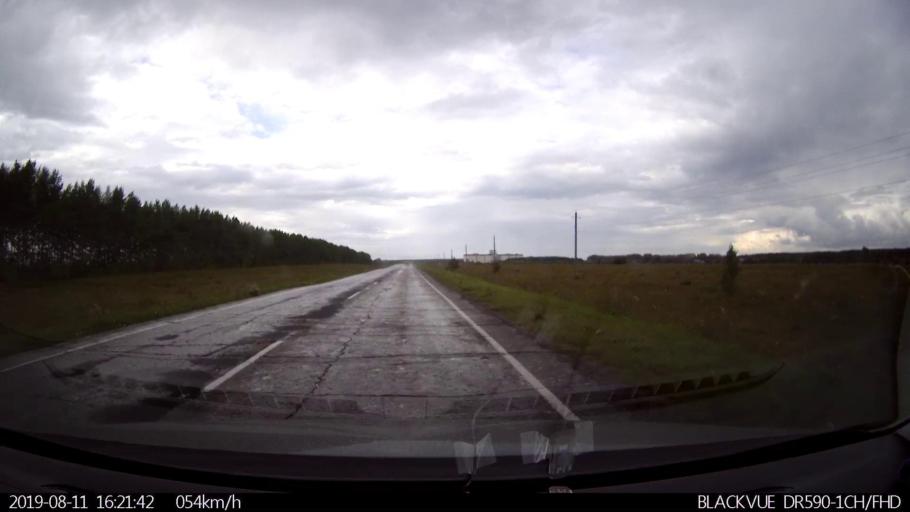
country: RU
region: Ulyanovsk
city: Mayna
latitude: 54.0819
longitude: 47.5967
